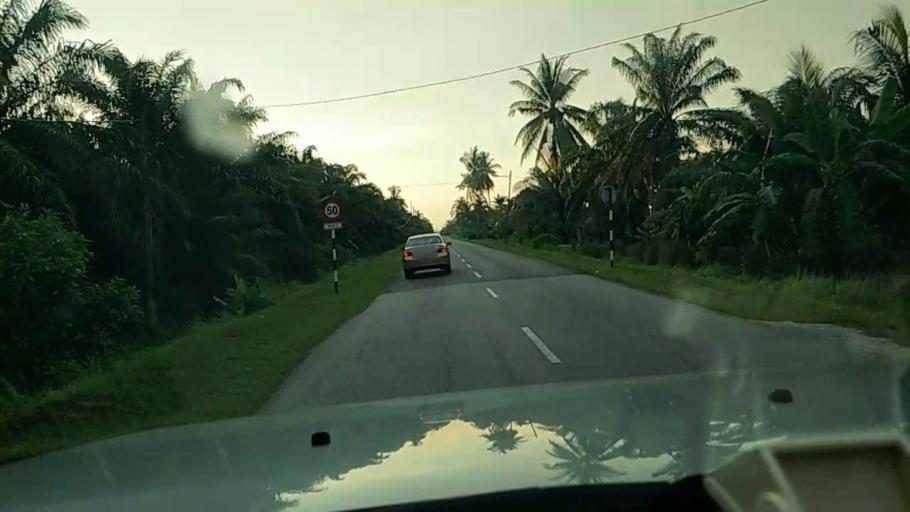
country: MY
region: Selangor
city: Kuala Selangor
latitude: 3.3139
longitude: 101.2843
